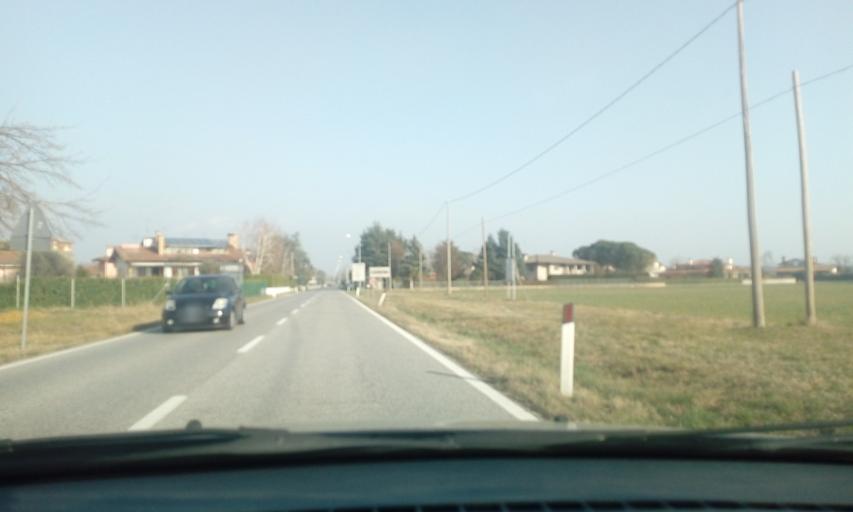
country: IT
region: Friuli Venezia Giulia
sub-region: Provincia di Gorizia
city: Cormons
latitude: 45.9526
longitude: 13.4578
